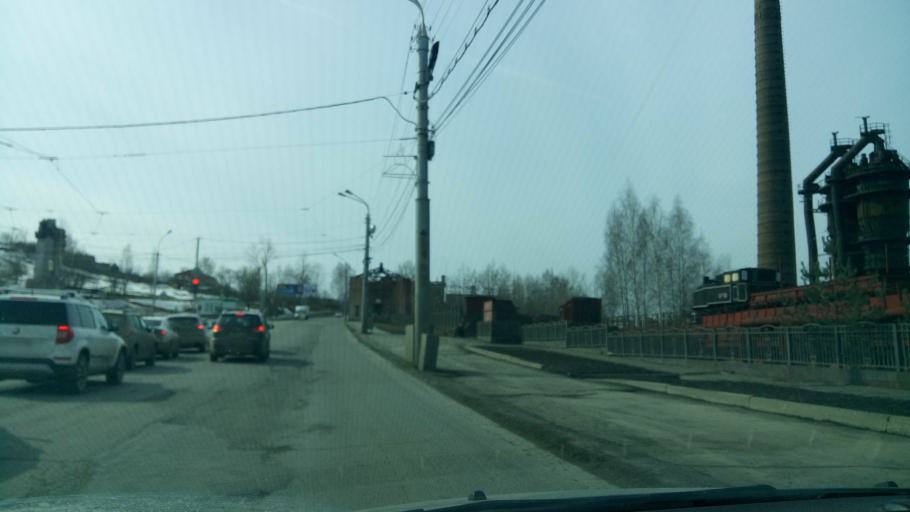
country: RU
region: Sverdlovsk
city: Nizhniy Tagil
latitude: 57.9036
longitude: 59.9482
